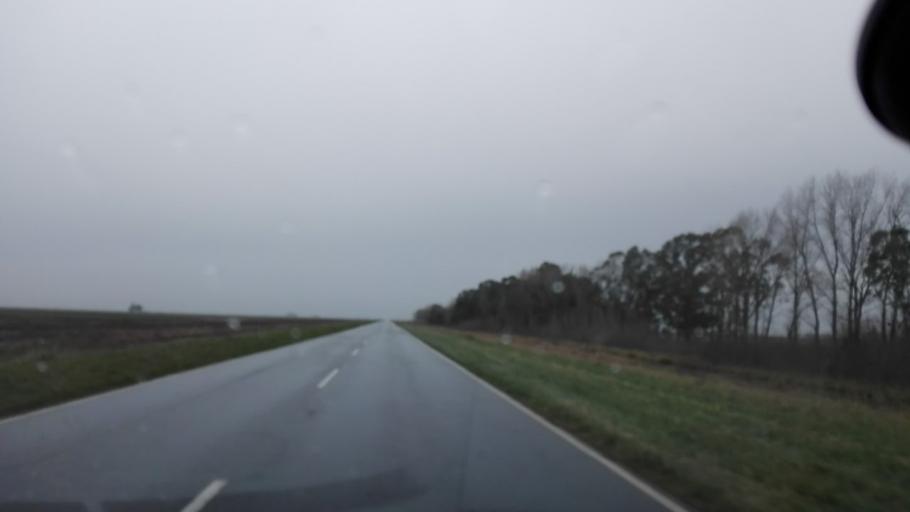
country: AR
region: Buenos Aires
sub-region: Partido de Tandil
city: Tandil
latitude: -37.0655
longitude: -58.9997
